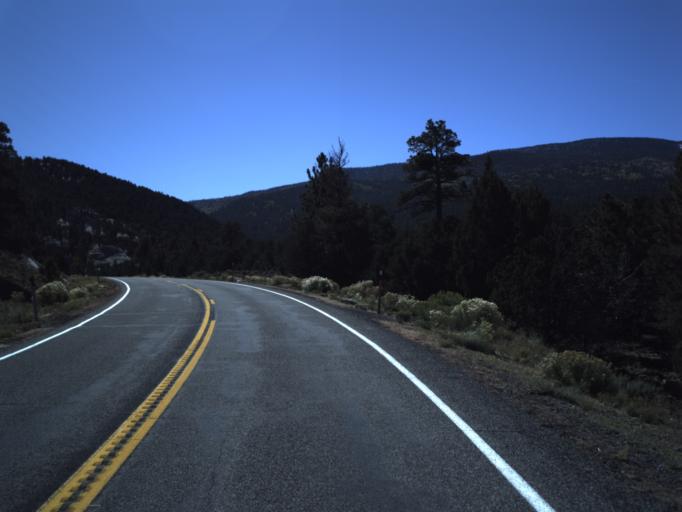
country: US
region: Utah
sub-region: Wayne County
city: Loa
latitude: 38.1973
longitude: -111.3518
